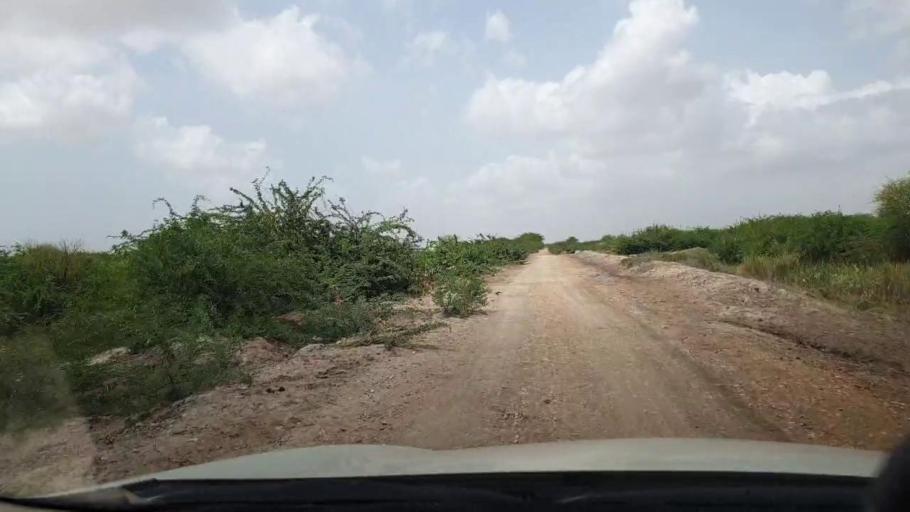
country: PK
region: Sindh
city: Kadhan
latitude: 24.3698
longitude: 68.8529
